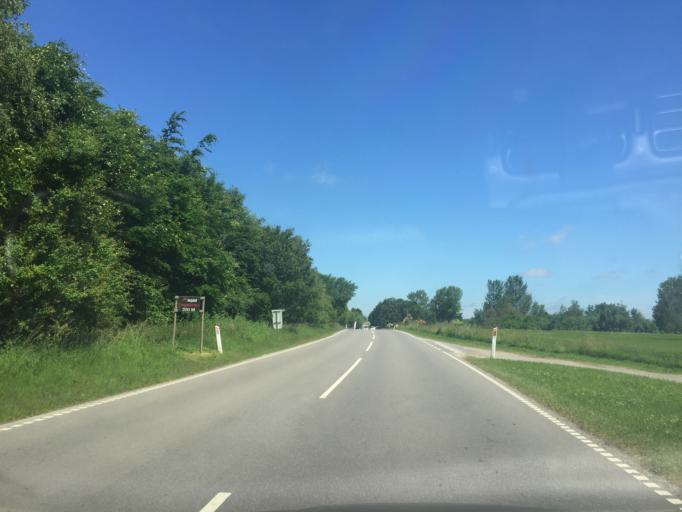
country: DK
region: Capital Region
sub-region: Hoje-Taastrup Kommune
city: Flong
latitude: 55.6656
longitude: 12.2077
